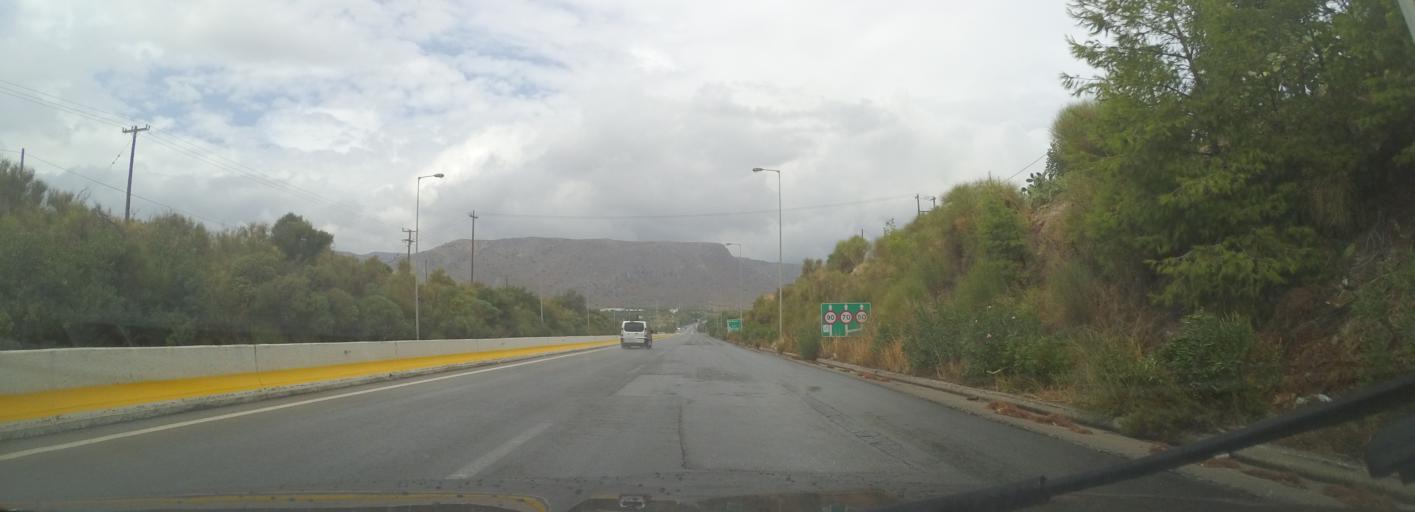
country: GR
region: Crete
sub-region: Nomos Irakleiou
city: Gazi
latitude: 35.3198
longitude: 25.0671
